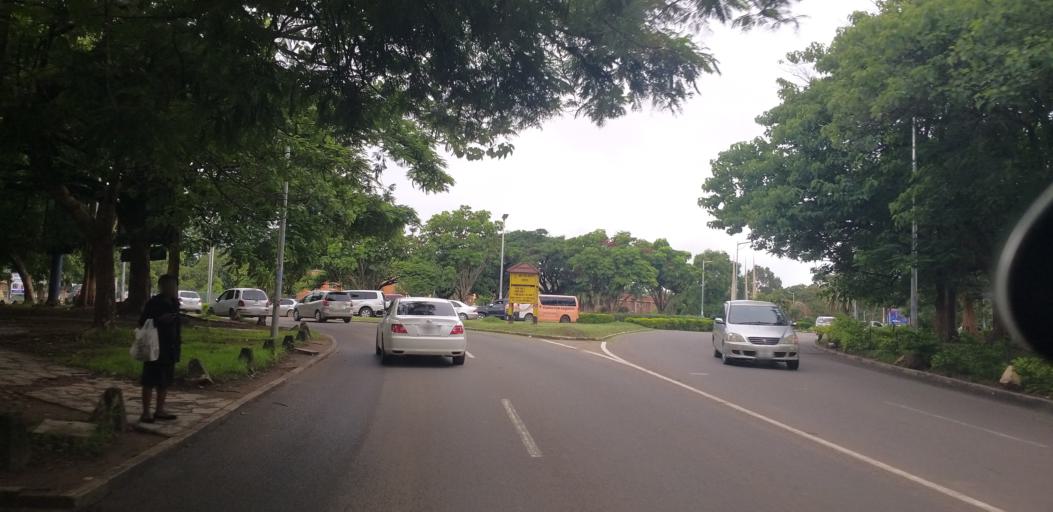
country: ZM
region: Lusaka
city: Lusaka
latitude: -15.4194
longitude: 28.3039
